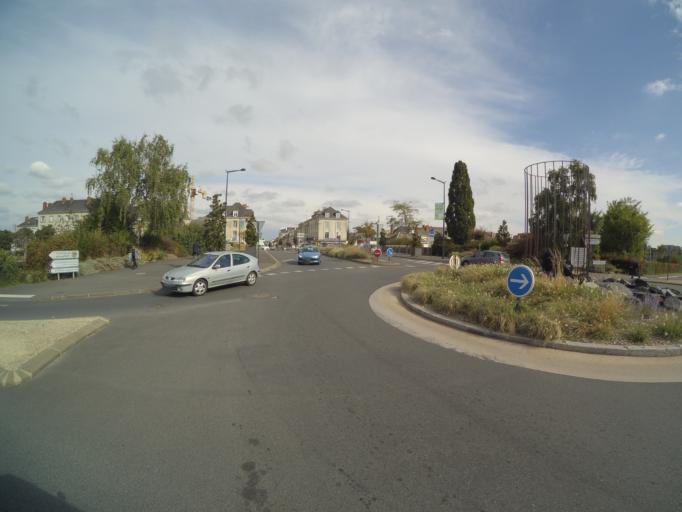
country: FR
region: Pays de la Loire
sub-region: Departement de Maine-et-Loire
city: Saumur
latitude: 47.2673
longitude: -0.0700
